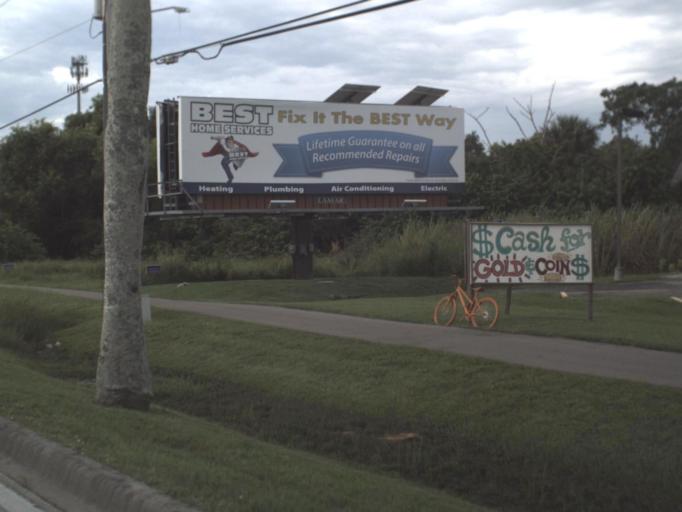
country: US
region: Florida
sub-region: Lee County
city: Harlem Heights
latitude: 26.5018
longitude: -81.9435
